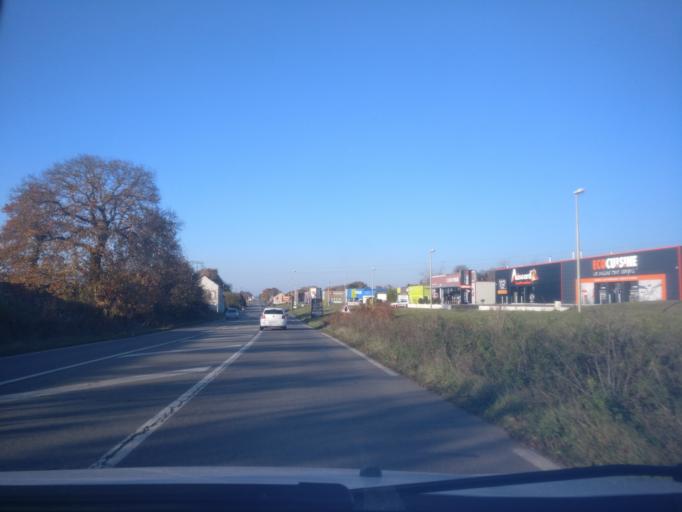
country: FR
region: Brittany
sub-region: Departement d'Ille-et-Vilaine
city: La Chapelle-des-Fougeretz
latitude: 48.1846
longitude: -1.7249
